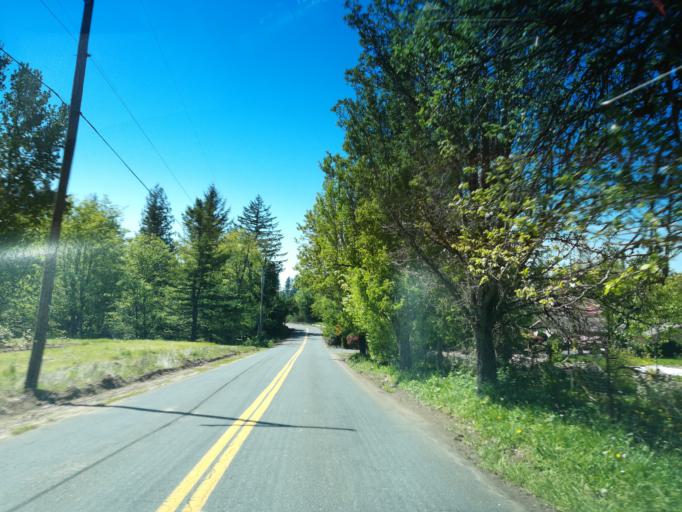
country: US
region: Oregon
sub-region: Multnomah County
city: Troutdale
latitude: 45.5119
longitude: -122.3601
